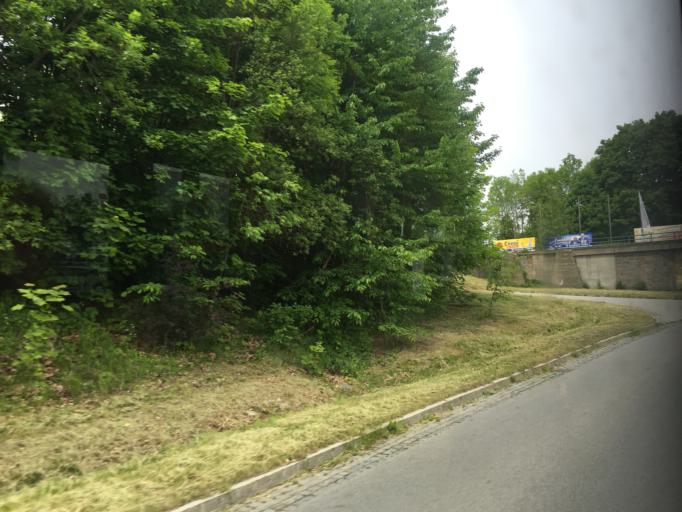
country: DE
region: Saxony
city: Lobau
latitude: 51.0995
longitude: 14.6745
